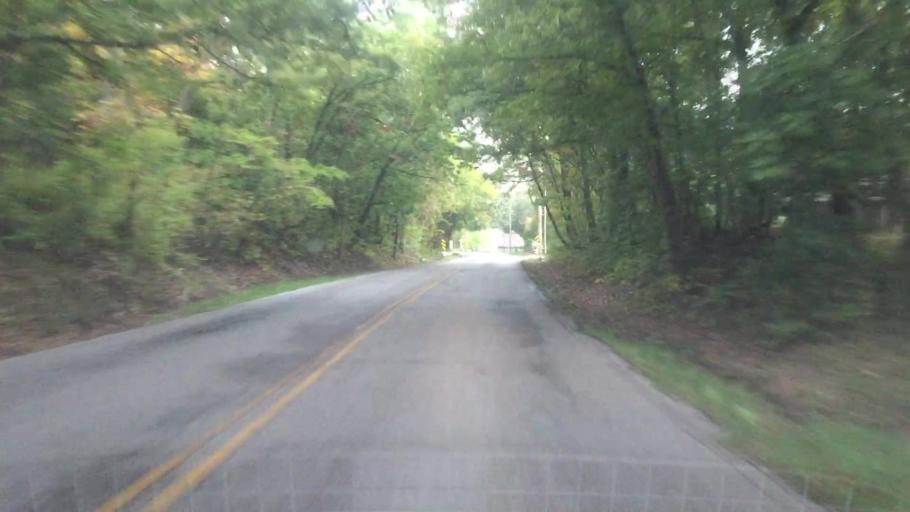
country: US
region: Kansas
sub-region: Johnson County
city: Shawnee
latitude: 39.0452
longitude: -94.7591
